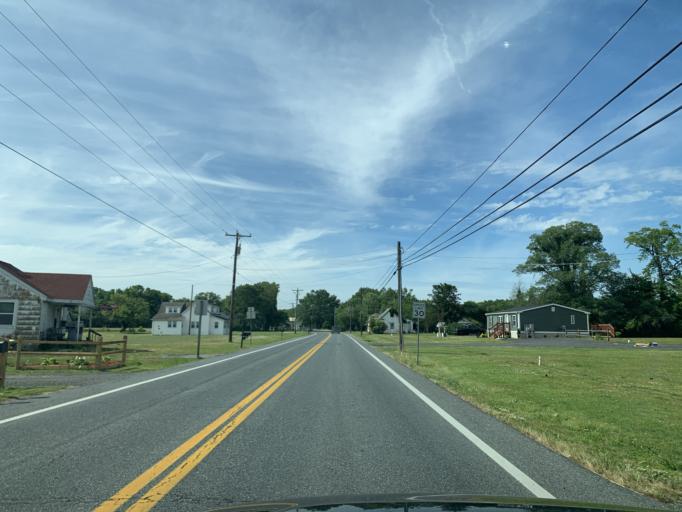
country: US
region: Maryland
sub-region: Wicomico County
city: Pittsville
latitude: 38.3249
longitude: -75.3738
